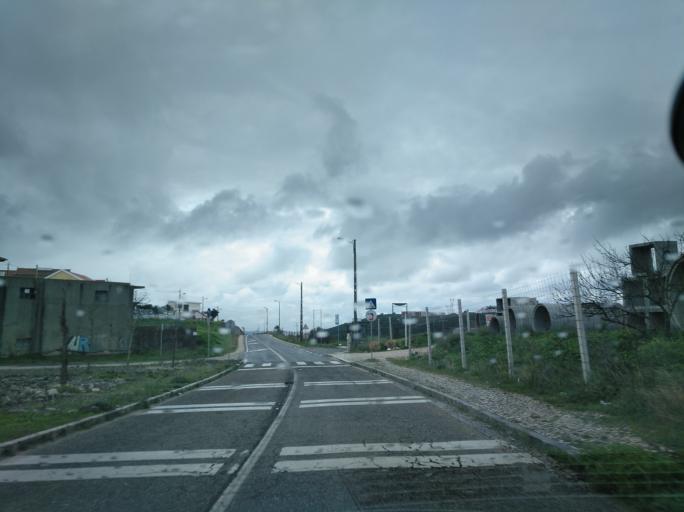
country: PT
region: Lisbon
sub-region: Odivelas
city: Canecas
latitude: 38.7954
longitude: -9.2299
